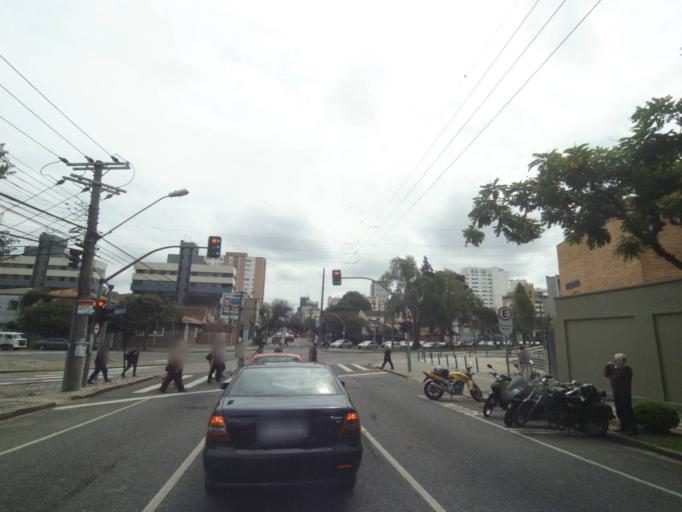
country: BR
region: Parana
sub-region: Curitiba
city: Curitiba
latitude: -25.4305
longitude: -49.2804
